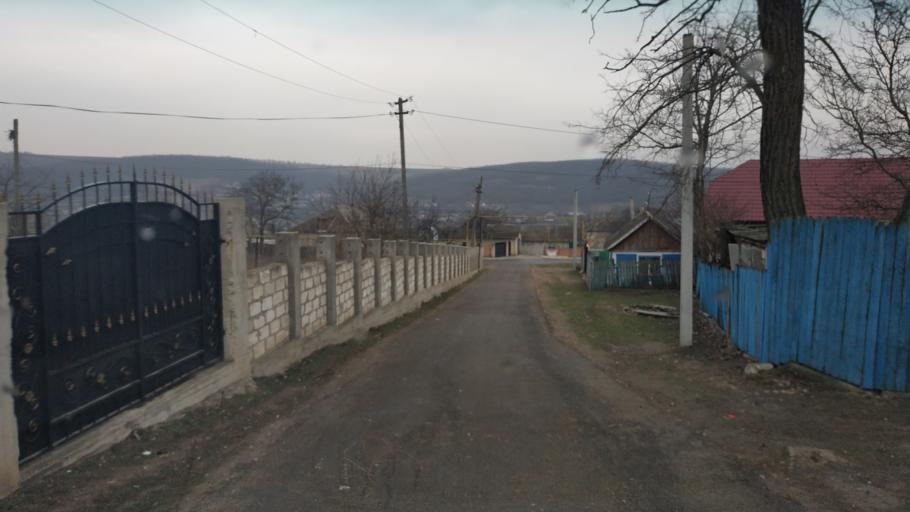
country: MD
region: Chisinau
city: Singera
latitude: 46.8312
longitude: 28.9718
